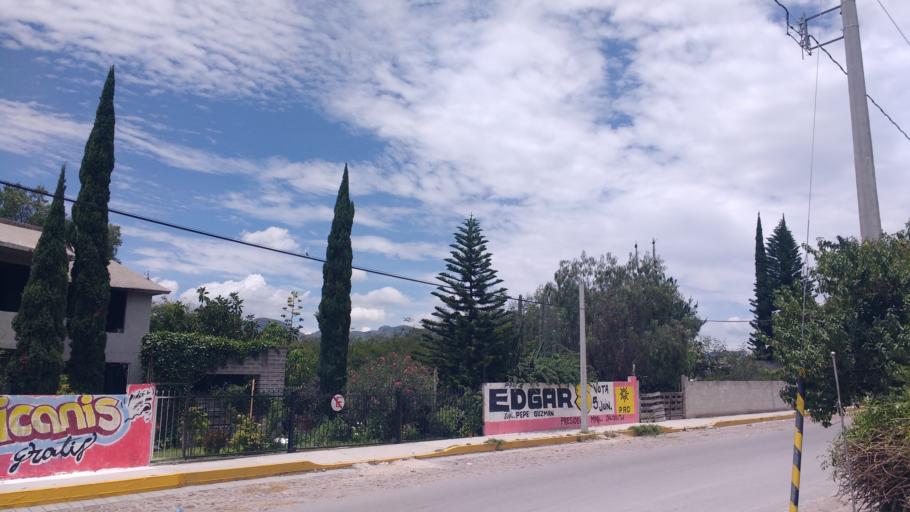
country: MX
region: Hidalgo
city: Mixquiahuala de Juarez
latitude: 20.2520
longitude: -99.2450
